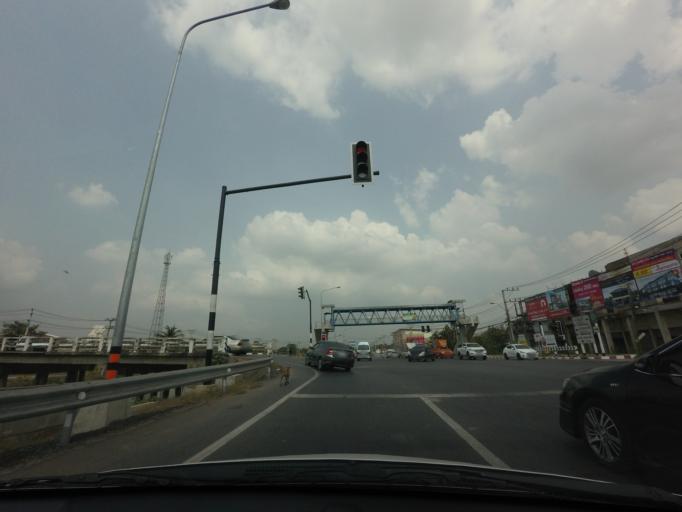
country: TH
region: Pathum Thani
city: Thanyaburi
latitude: 14.0669
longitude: 100.7102
